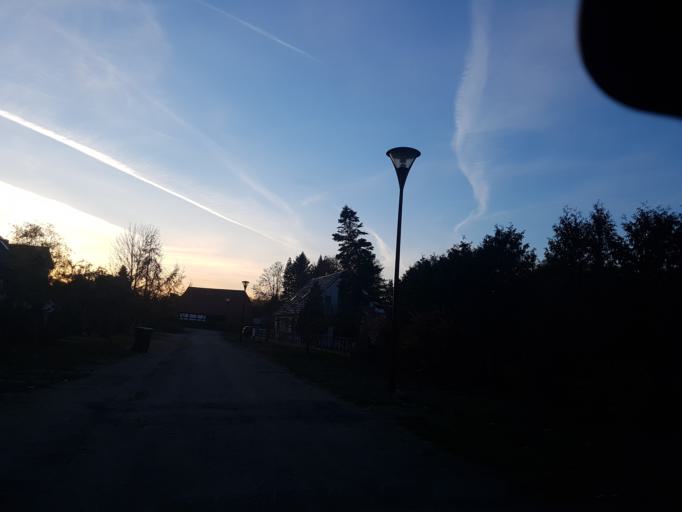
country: DE
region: Brandenburg
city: Finsterwalde
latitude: 51.6422
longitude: 13.6857
